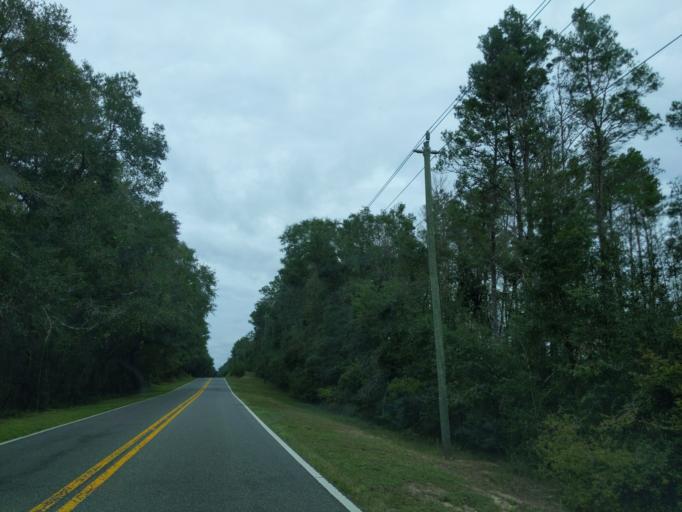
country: US
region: Florida
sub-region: Leon County
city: Woodville
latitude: 30.3685
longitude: -84.1760
